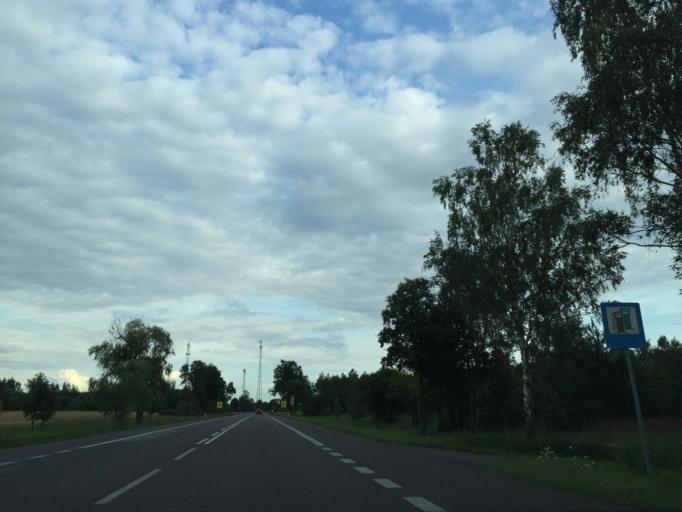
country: PL
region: Lublin Voivodeship
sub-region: Powiat lubartowski
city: Firlej
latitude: 51.5689
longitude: 22.5005
